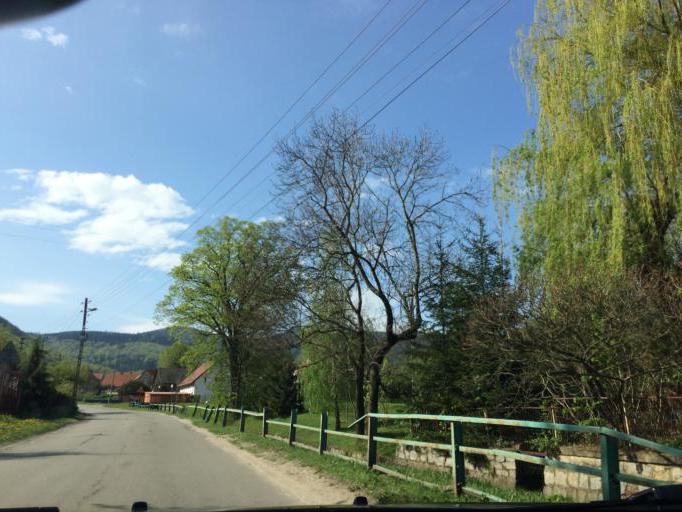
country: PL
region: Lower Silesian Voivodeship
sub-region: Powiat dzierzoniowski
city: Pieszyce
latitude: 50.6812
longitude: 16.5434
